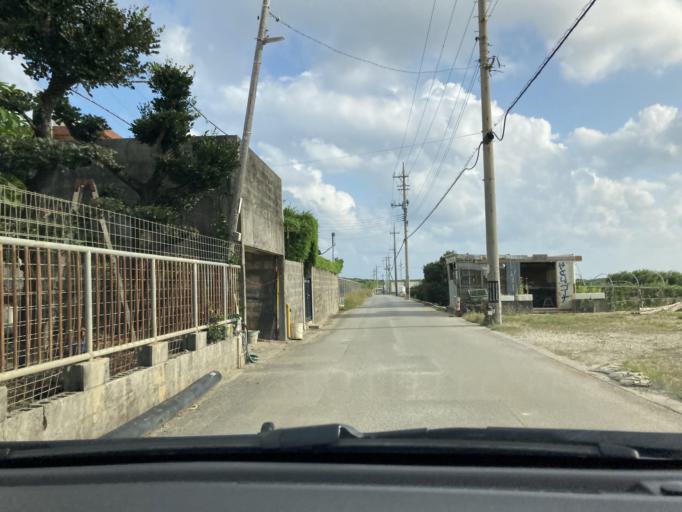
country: JP
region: Okinawa
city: Itoman
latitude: 26.0882
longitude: 127.6617
